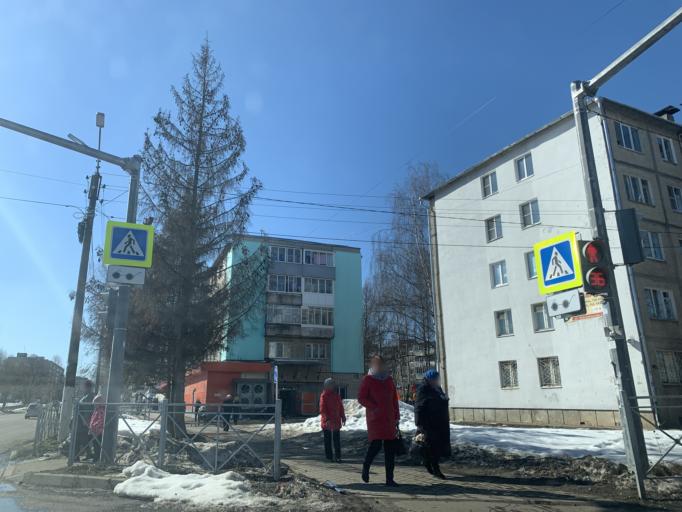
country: RU
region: Jaroslavl
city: Tutayev
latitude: 57.8701
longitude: 39.5140
